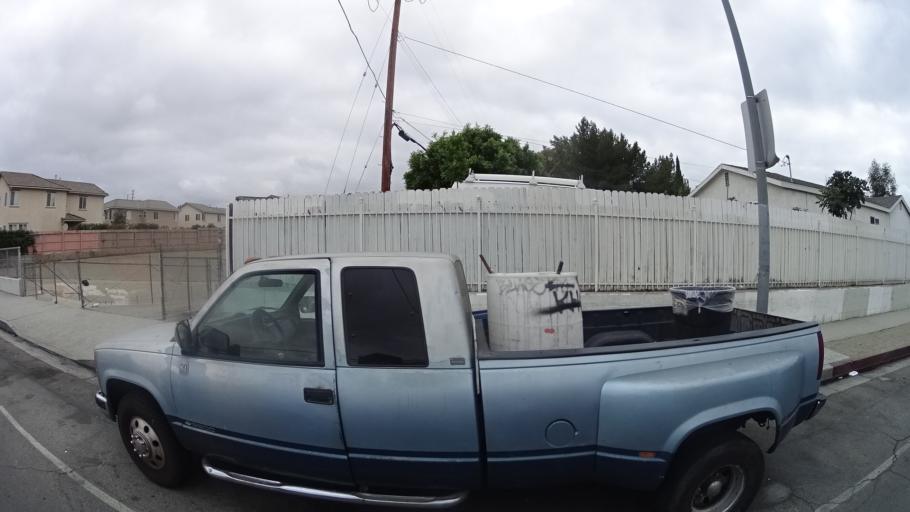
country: US
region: California
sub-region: Los Angeles County
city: Van Nuys
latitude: 34.2355
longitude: -118.4574
